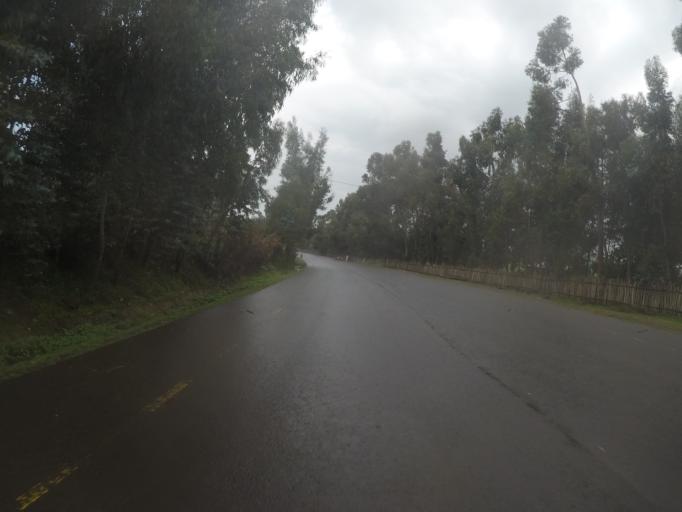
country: ET
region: Amhara
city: Debark'
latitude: 13.1071
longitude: 37.8592
